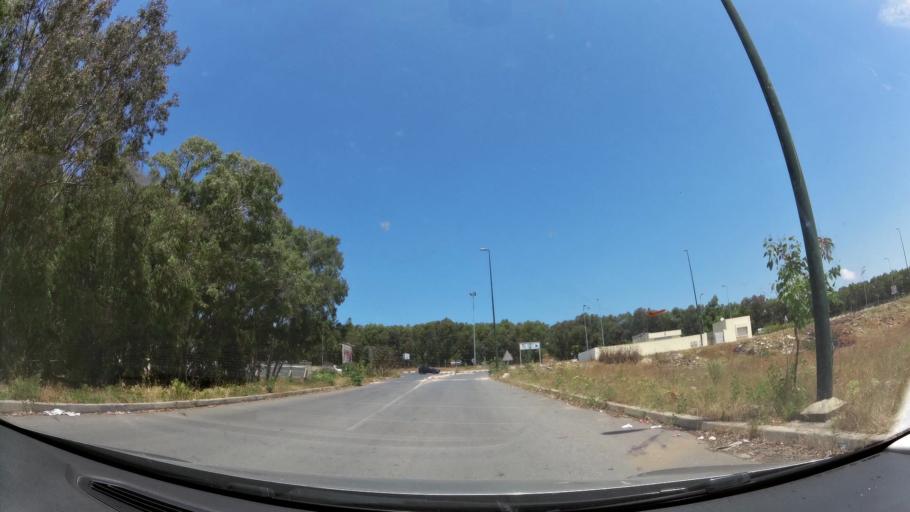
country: MA
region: Gharb-Chrarda-Beni Hssen
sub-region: Kenitra Province
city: Kenitra
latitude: 34.2709
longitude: -6.6328
